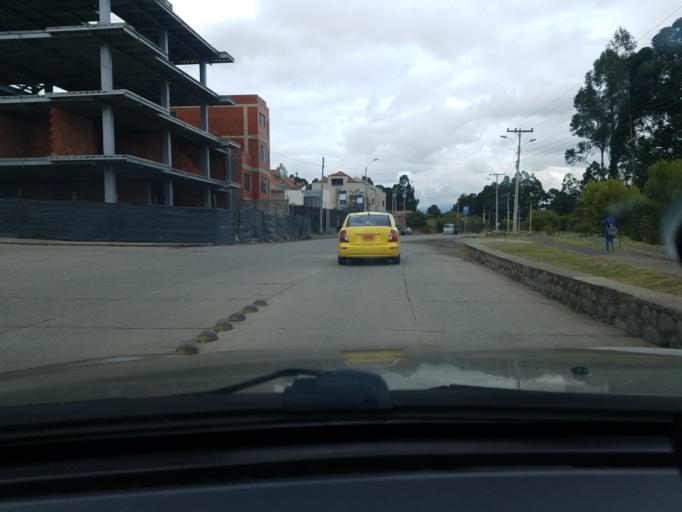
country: EC
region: Azuay
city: Cuenca
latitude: -2.8932
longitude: -78.9633
